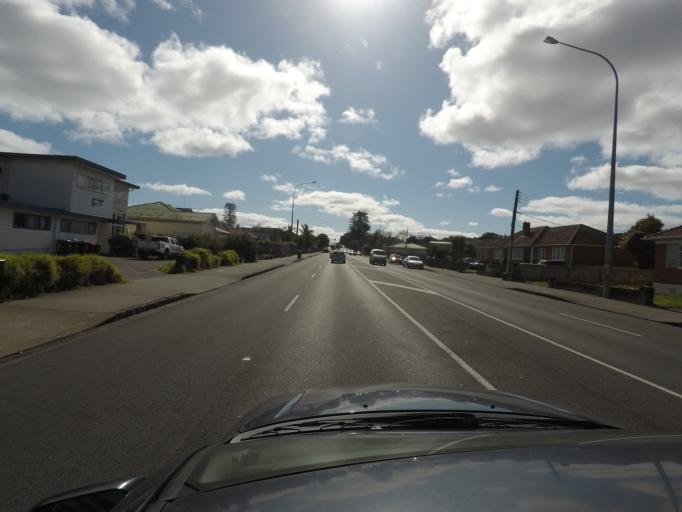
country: NZ
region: Auckland
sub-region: Auckland
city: Rosebank
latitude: -36.8910
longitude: 174.7084
